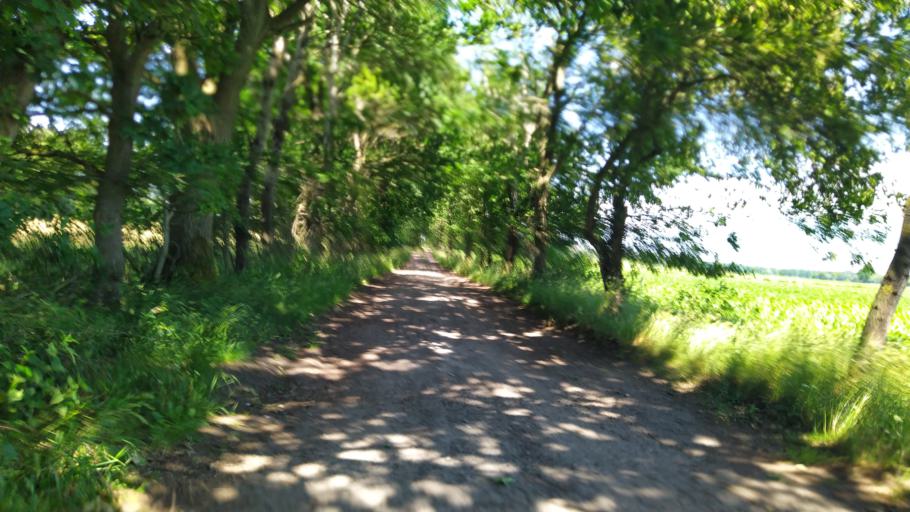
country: DE
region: Lower Saxony
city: Heinbockel
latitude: 53.5516
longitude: 9.2860
